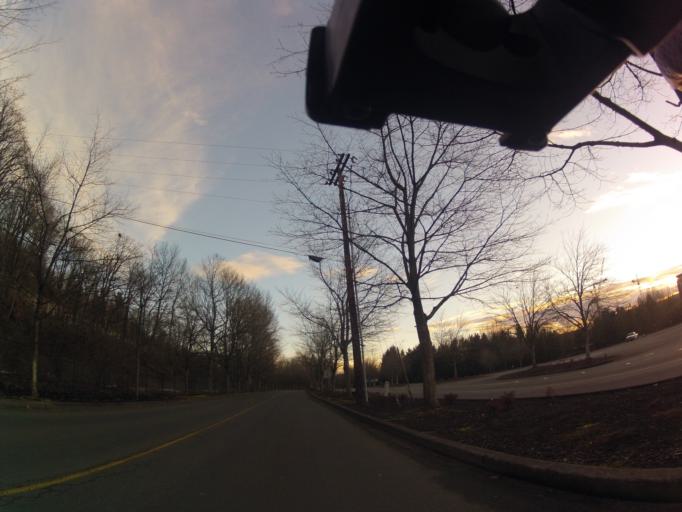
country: US
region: Washington
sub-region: King County
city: Renton
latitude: 47.5071
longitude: -122.2014
